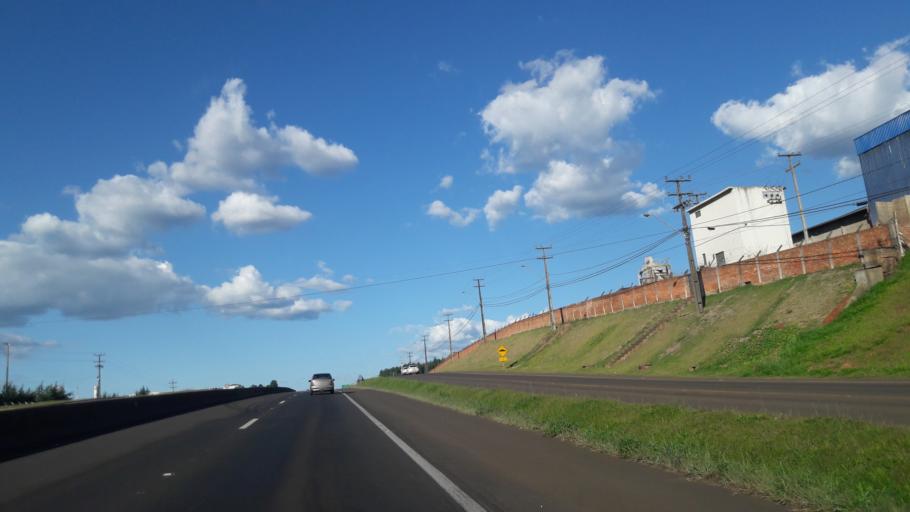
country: BR
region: Parana
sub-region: Guarapuava
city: Guarapuava
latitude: -25.3548
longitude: -51.4609
